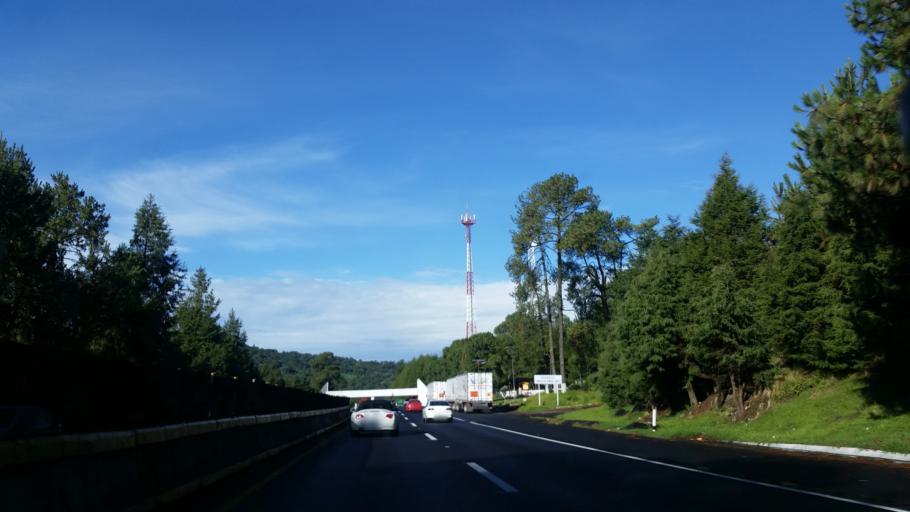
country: MX
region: Morelos
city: Tres Marias
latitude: 19.0910
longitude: -99.2144
